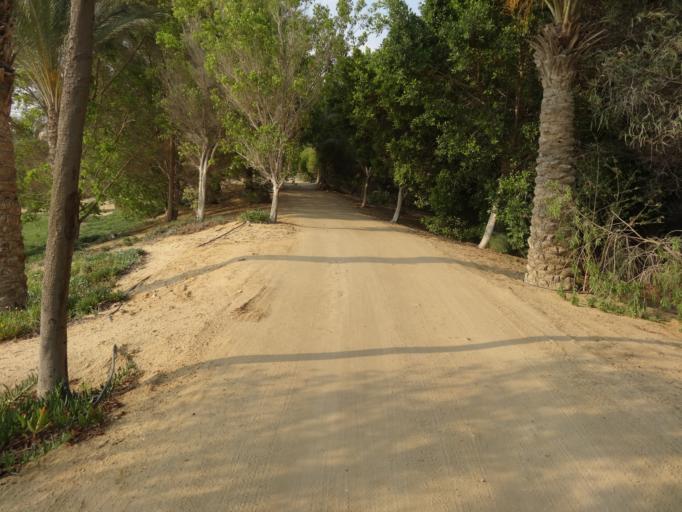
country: EG
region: Muhafazat al Qalyubiyah
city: Al Khankah
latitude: 30.0676
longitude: 31.4343
